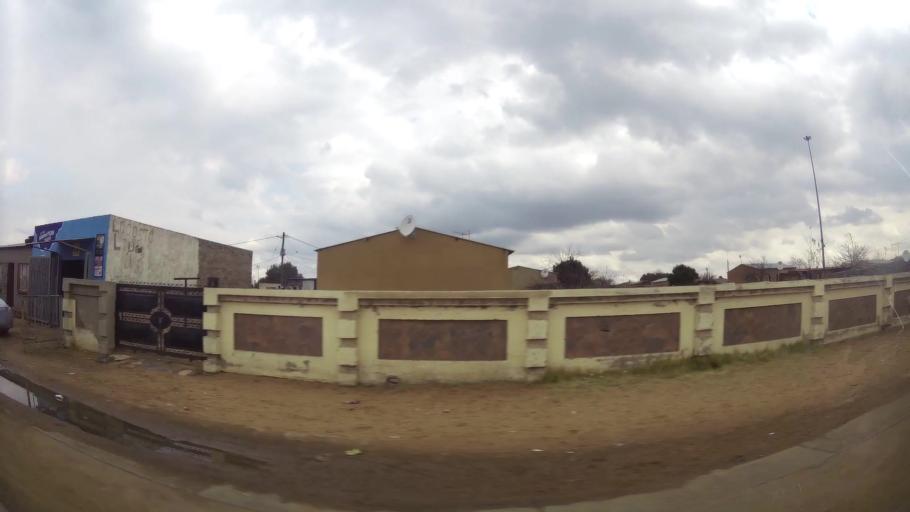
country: ZA
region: Orange Free State
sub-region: Fezile Dabi District Municipality
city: Sasolburg
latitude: -26.8580
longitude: 27.8794
